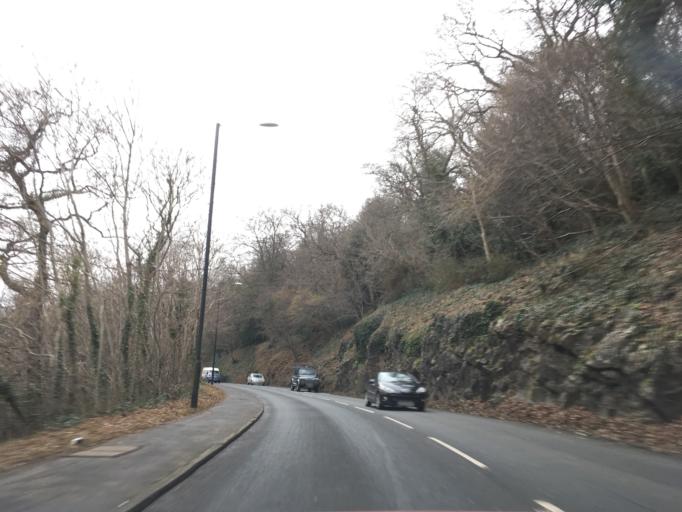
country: GB
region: England
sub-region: Bristol
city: Bristol
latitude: 51.4592
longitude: -2.6292
